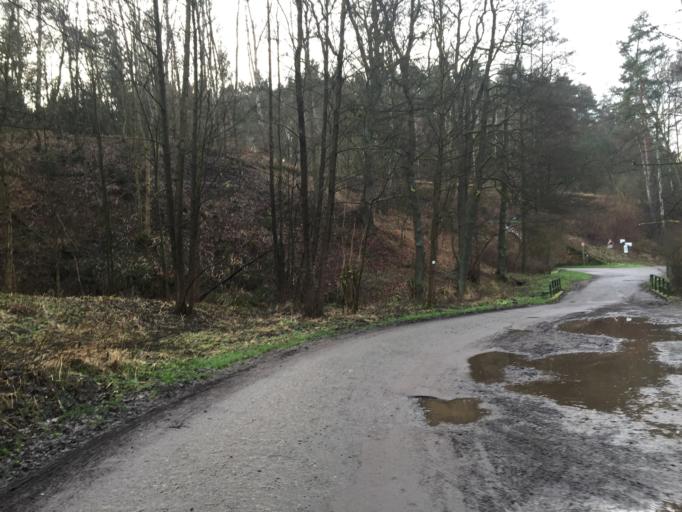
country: DE
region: Thuringia
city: Schleifreisen
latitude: 50.8931
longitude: 11.8208
